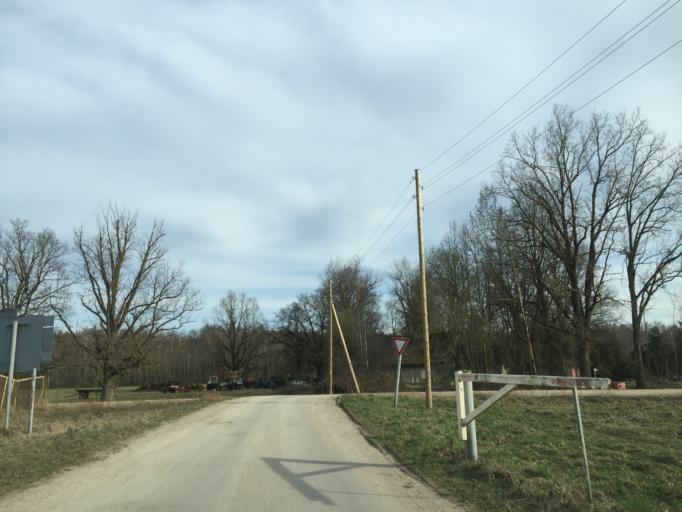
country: LV
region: Ogre
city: Ogre
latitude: 56.7822
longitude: 24.6609
